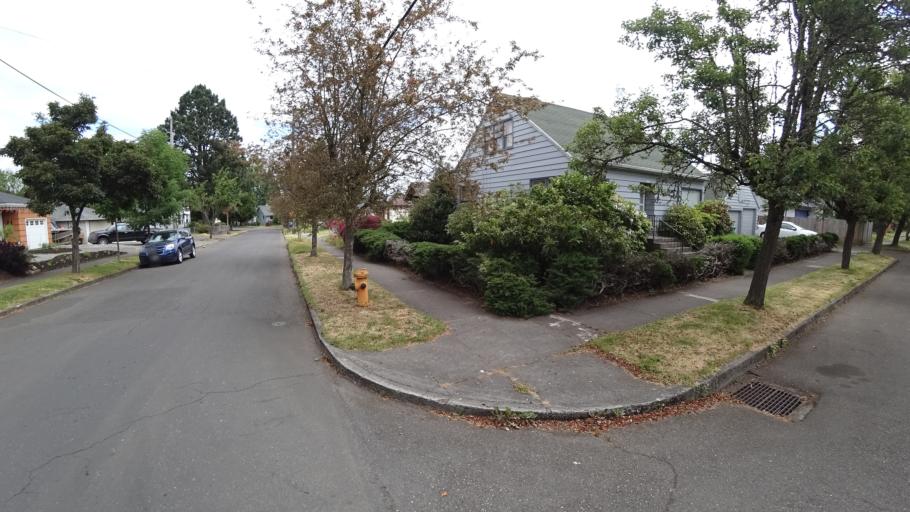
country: US
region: Oregon
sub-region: Multnomah County
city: Portland
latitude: 45.5857
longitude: -122.7259
